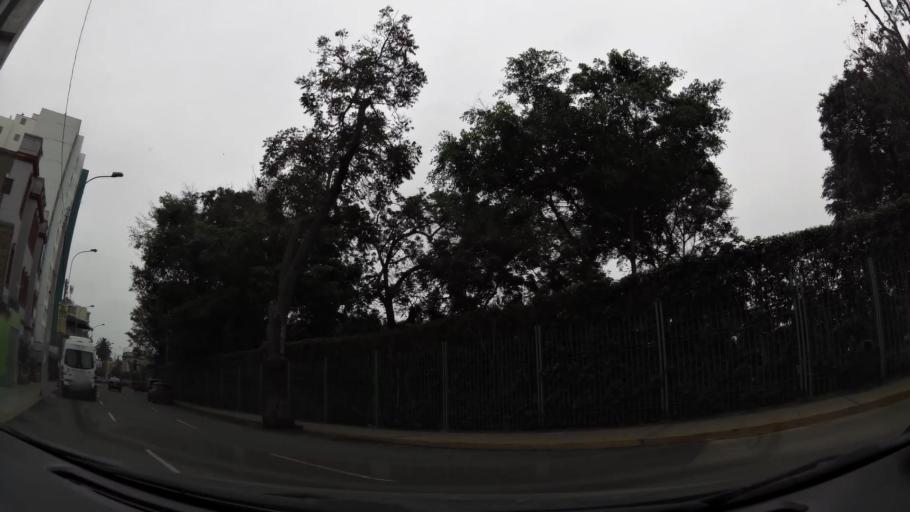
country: PE
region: Lima
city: Lima
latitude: -12.0722
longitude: -77.0335
